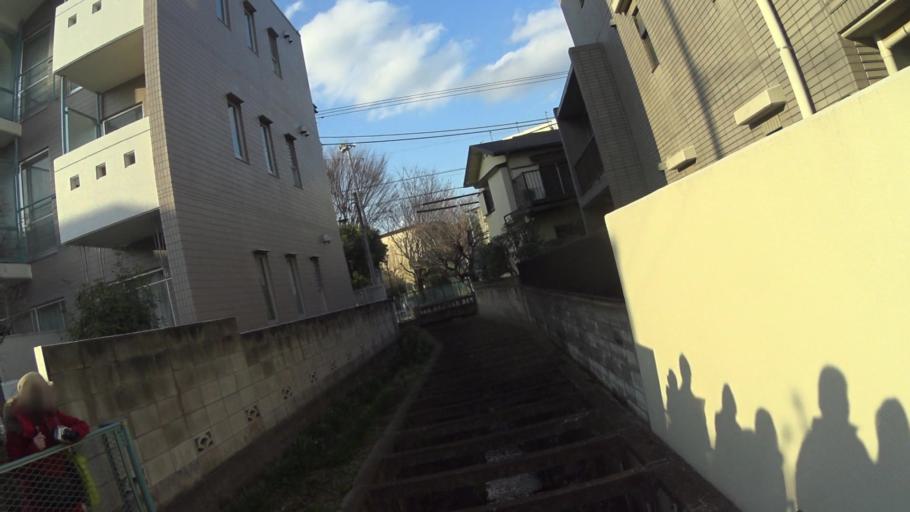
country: JP
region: Tokyo
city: Chofugaoka
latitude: 35.6421
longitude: 139.6122
